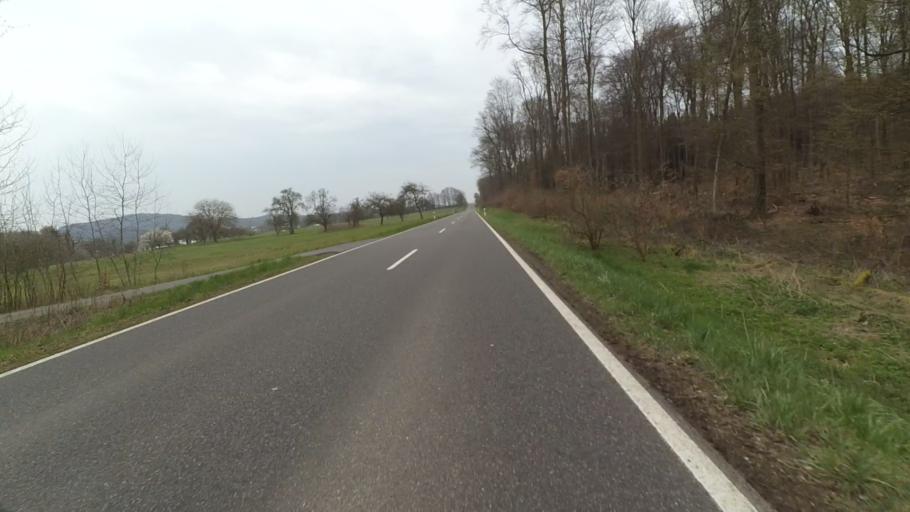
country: DE
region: Rheinland-Pfalz
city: Quirnbach
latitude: 50.5148
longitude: 7.8027
